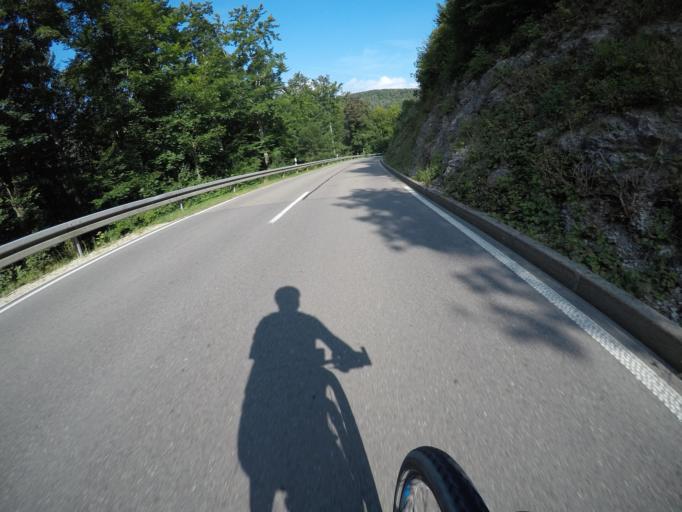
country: DE
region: Baden-Wuerttemberg
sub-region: Regierungsbezirk Stuttgart
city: Geislingen an der Steige
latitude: 48.6372
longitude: 9.8786
